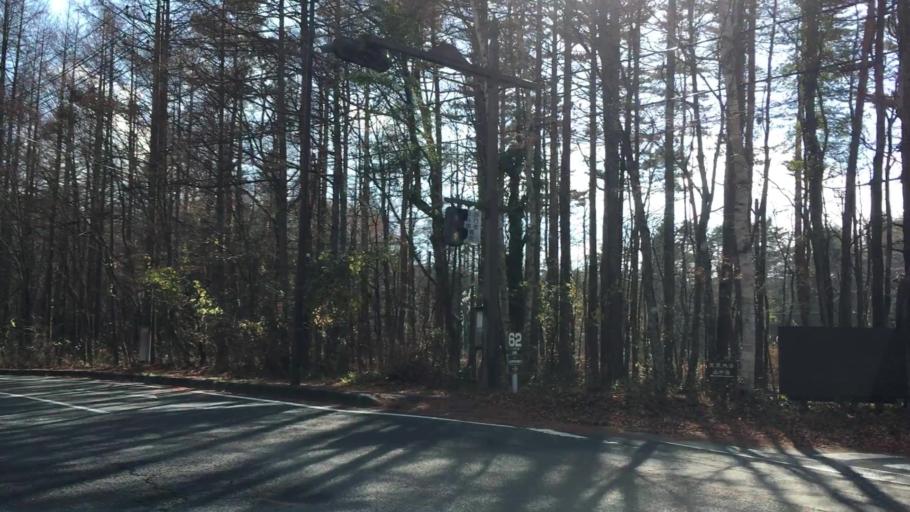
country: JP
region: Shizuoka
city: Gotemba
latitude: 35.4102
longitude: 138.8623
